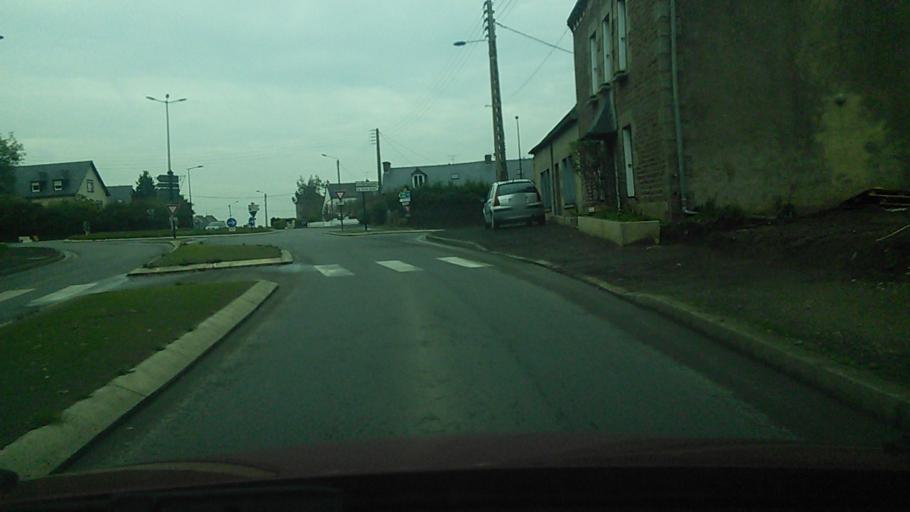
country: FR
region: Brittany
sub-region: Departement des Cotes-d'Armor
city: Pommeret
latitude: 48.4700
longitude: -2.6503
